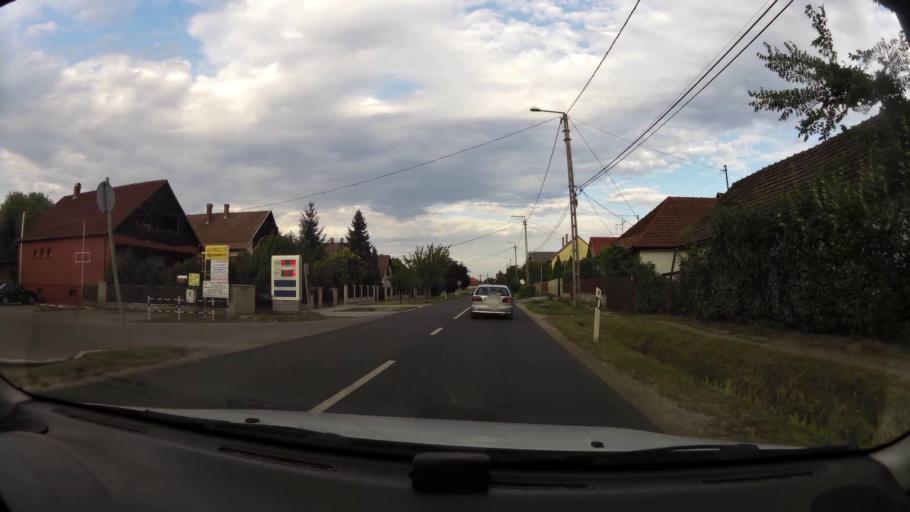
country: HU
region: Pest
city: Suelysap
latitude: 47.4486
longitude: 19.5325
